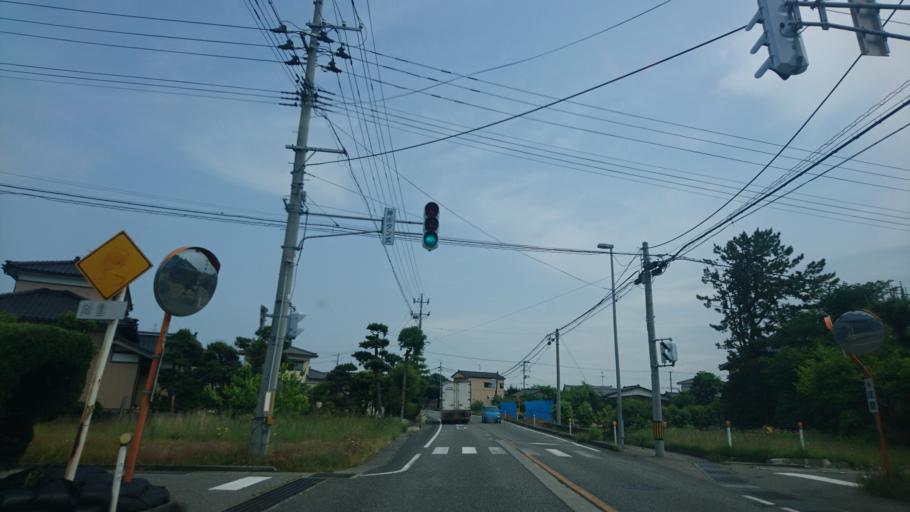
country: JP
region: Niigata
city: Shibata
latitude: 38.0130
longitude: 139.2795
